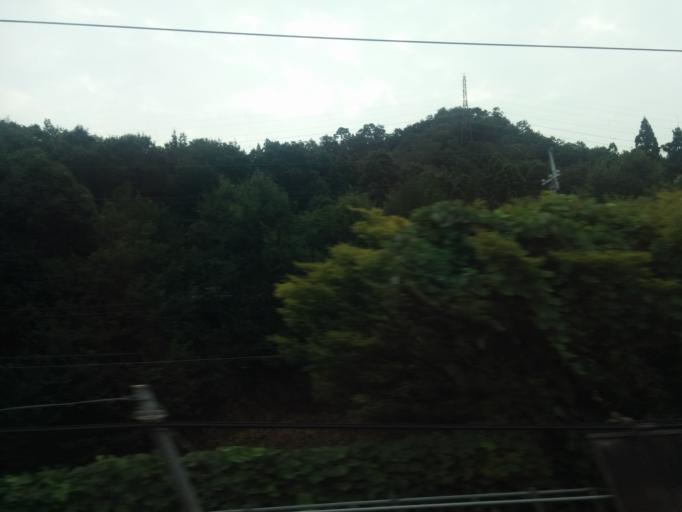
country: JP
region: Shiga Prefecture
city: Hikone
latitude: 35.2646
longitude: 136.2787
